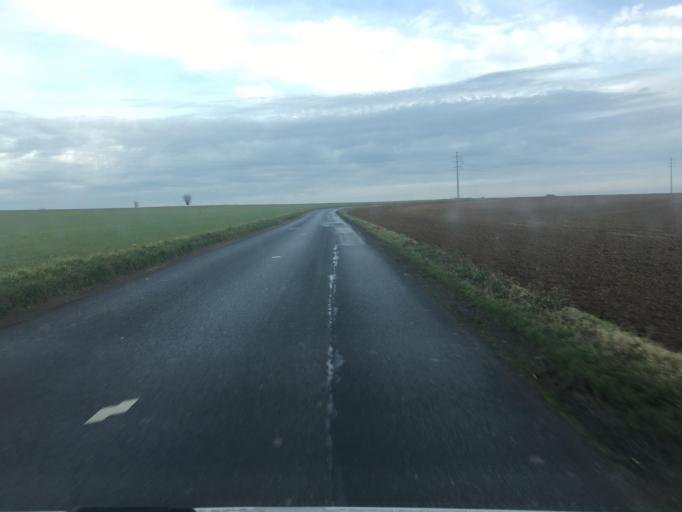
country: FR
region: Lower Normandy
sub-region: Departement du Calvados
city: Creully
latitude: 49.2589
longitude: -0.5618
